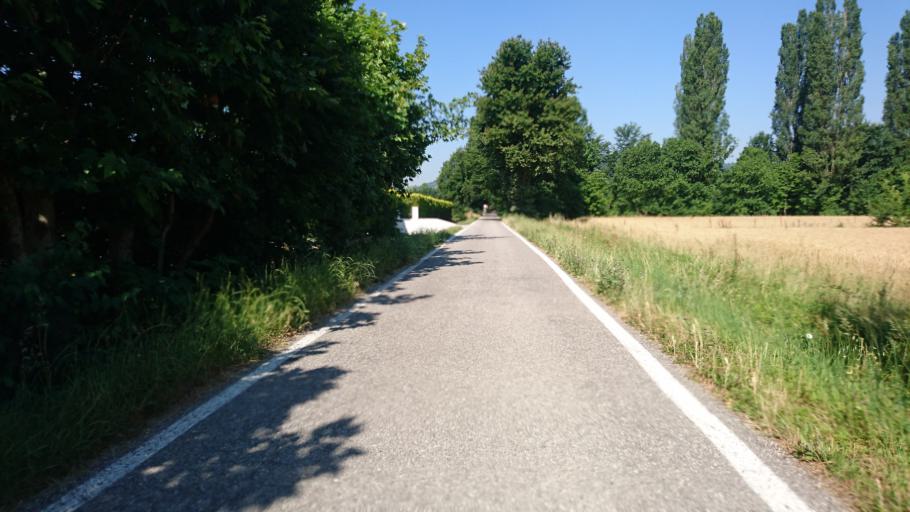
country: IT
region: Veneto
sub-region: Provincia di Padova
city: San Biagio
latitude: 45.3580
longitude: 11.7565
